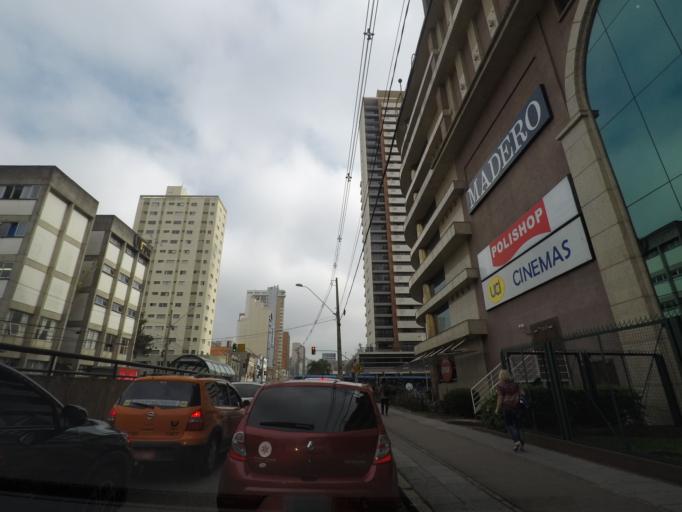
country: BR
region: Parana
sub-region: Curitiba
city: Curitiba
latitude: -25.4388
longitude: -49.2680
